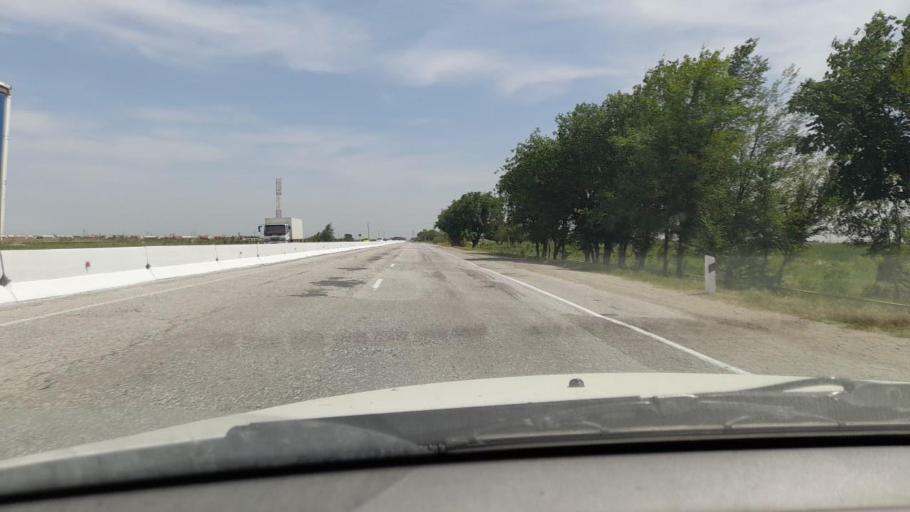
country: UZ
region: Navoiy
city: Konimex
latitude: 40.1112
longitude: 65.0710
